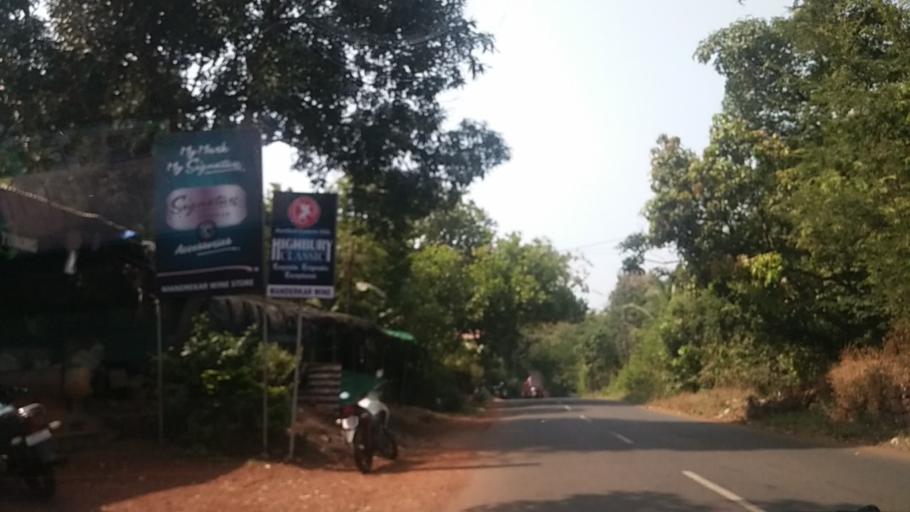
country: IN
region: Goa
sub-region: North Goa
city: Morjim
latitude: 15.6607
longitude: 73.7405
